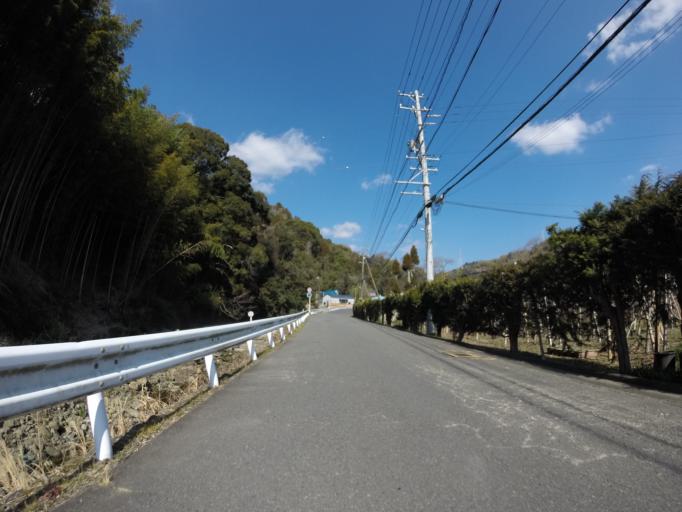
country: JP
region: Shizuoka
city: Shizuoka-shi
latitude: 35.0677
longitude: 138.4834
